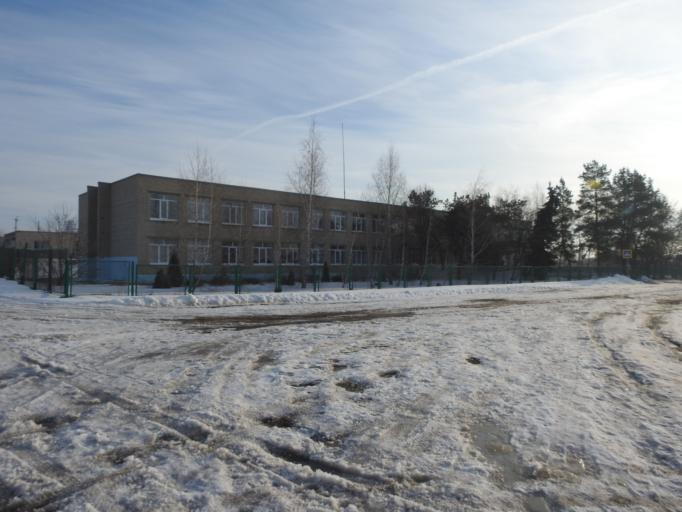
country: RU
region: Saratov
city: Krasnyy Oktyabr'
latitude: 51.4969
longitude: 45.7168
